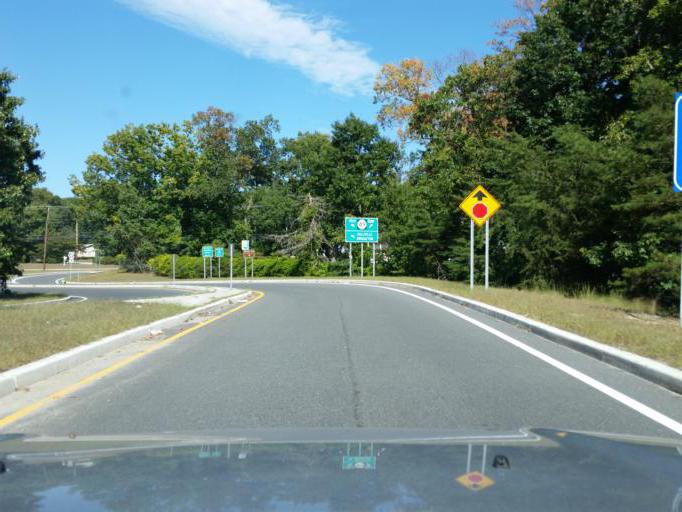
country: US
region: New Jersey
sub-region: Cumberland County
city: Millville
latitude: 39.3909
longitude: -75.0094
